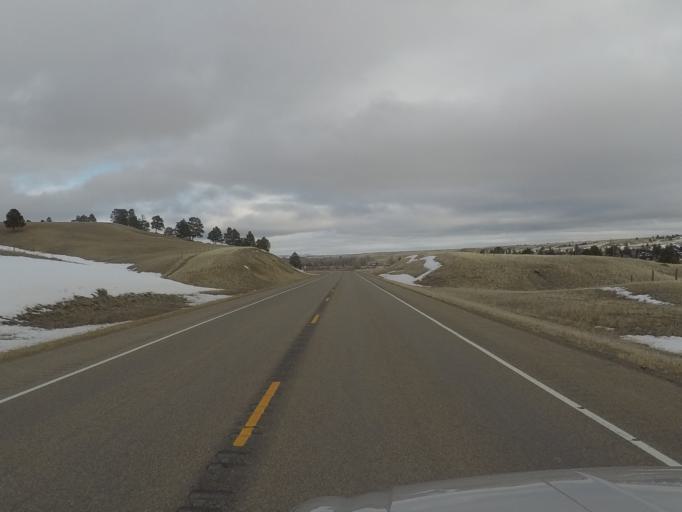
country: US
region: Montana
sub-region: Golden Valley County
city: Ryegate
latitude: 46.3213
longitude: -109.4412
